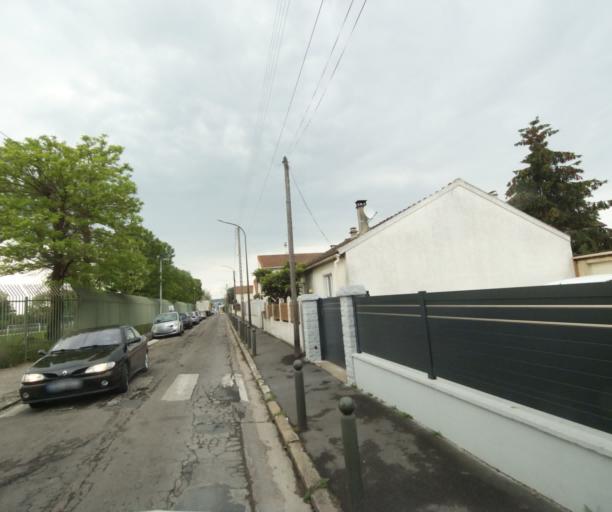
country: FR
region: Ile-de-France
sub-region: Departement du Val-d'Oise
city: Bezons
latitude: 48.9430
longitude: 2.2168
